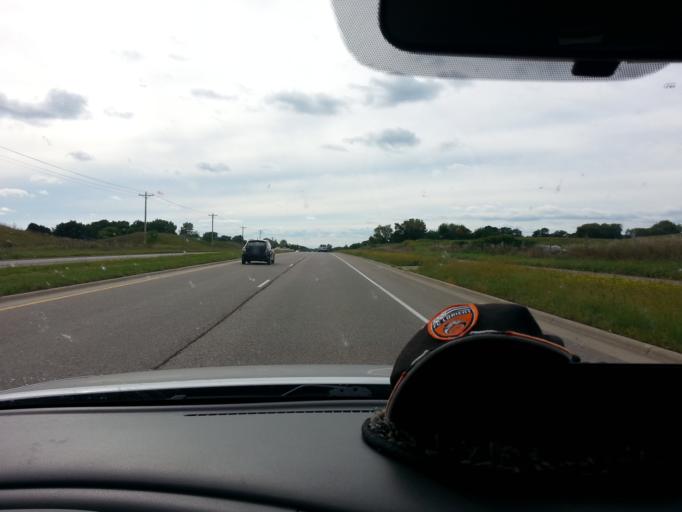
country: US
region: Minnesota
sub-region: Dakota County
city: Lakeville
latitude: 44.6815
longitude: -93.3224
